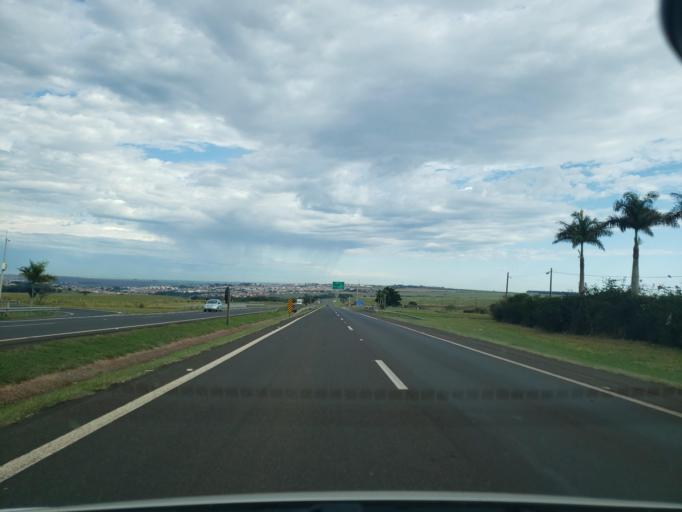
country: BR
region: Sao Paulo
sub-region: Jau
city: Jau
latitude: -22.2659
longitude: -48.5126
